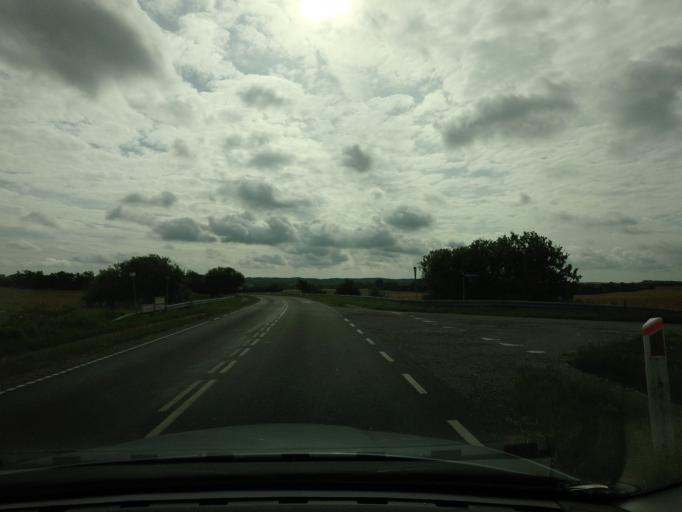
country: DK
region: North Denmark
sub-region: Bronderslev Kommune
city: Hjallerup
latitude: 57.2703
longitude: 10.1521
